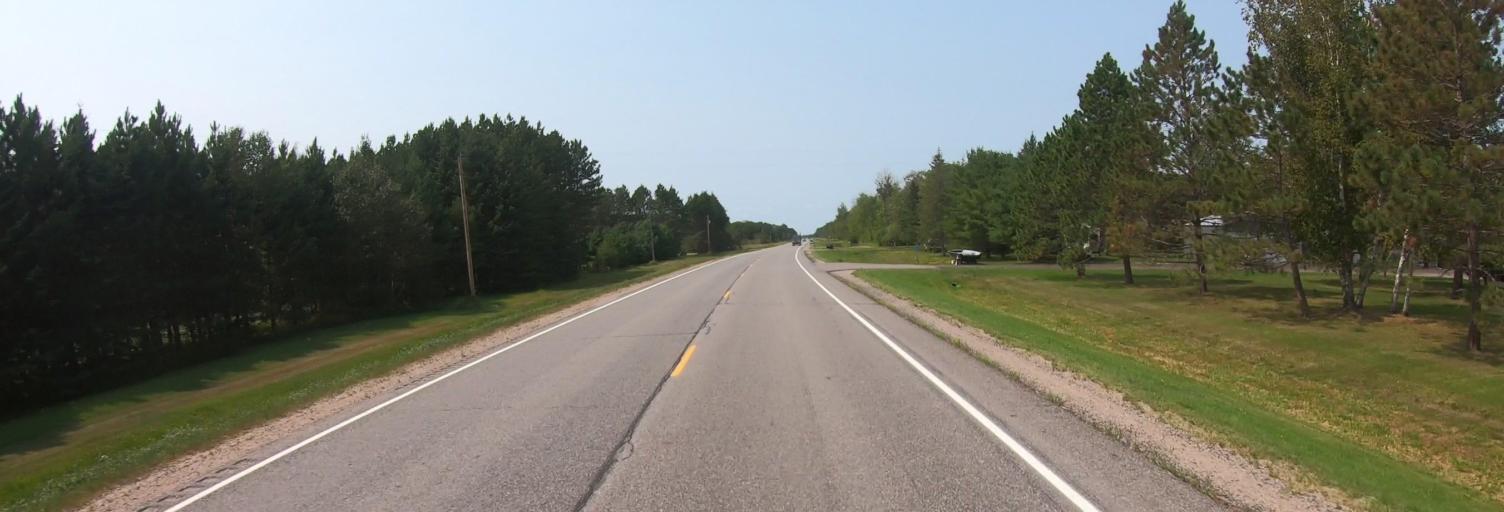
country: US
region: Minnesota
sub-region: Koochiching County
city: International Falls
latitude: 48.5190
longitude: -93.5992
